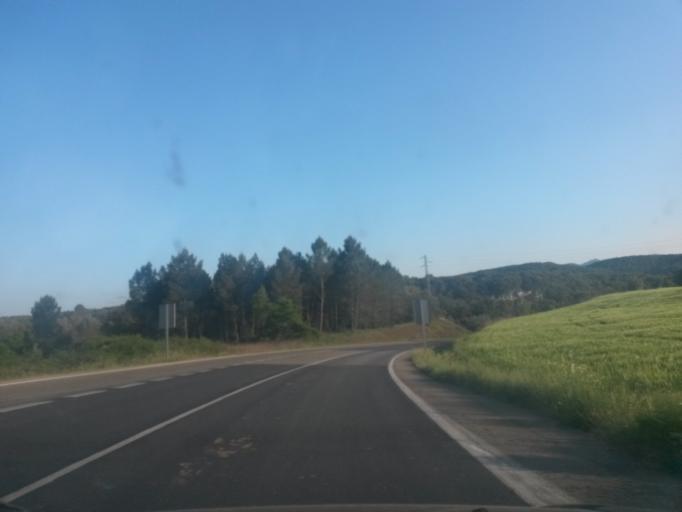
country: ES
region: Catalonia
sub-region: Provincia de Girona
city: Besalu
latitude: 42.1800
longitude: 2.7441
